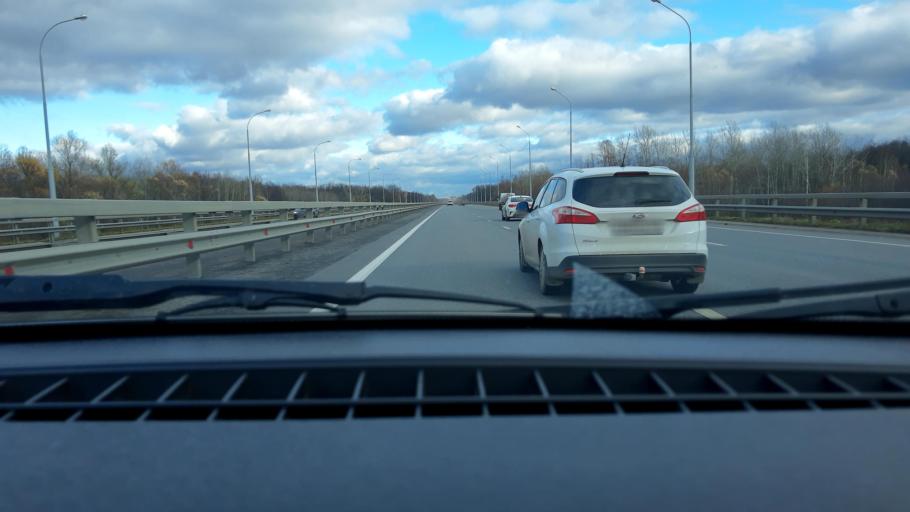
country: RU
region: Bashkortostan
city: Ufa
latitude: 54.6472
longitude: 56.0174
